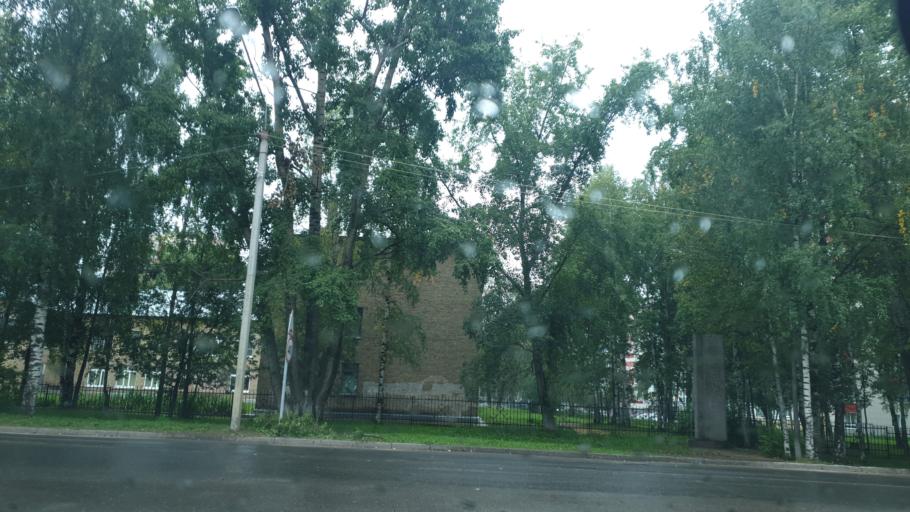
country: RU
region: Komi Republic
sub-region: Syktyvdinskiy Rayon
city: Syktyvkar
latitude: 61.6585
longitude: 50.8297
